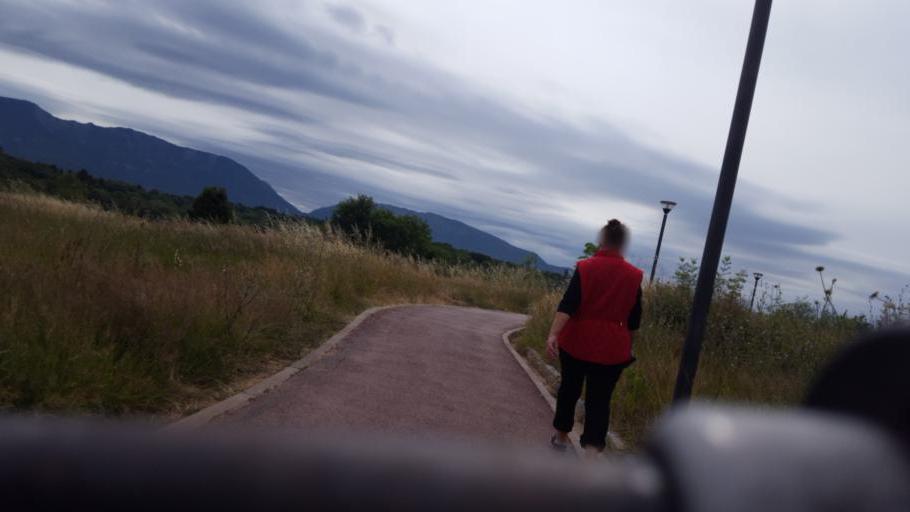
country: AL
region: Tirane
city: Tirana
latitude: 41.3083
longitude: 19.8171
